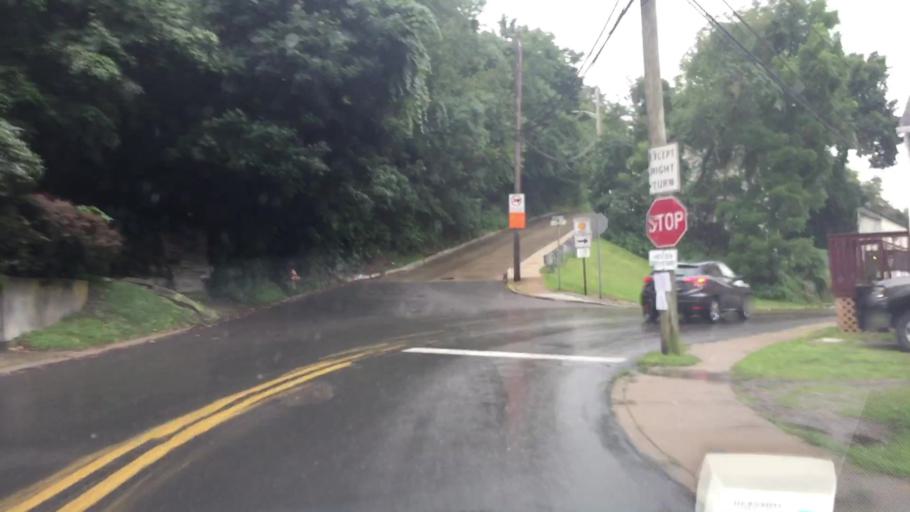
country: US
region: Pennsylvania
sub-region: Allegheny County
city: Bridgeville
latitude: 40.3573
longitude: -80.1052
